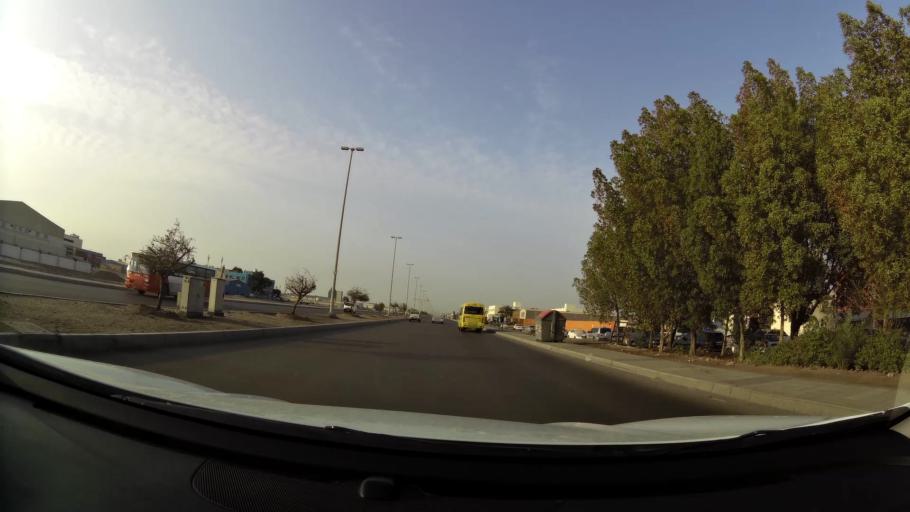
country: AE
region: Abu Dhabi
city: Abu Dhabi
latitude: 24.3618
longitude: 54.5018
